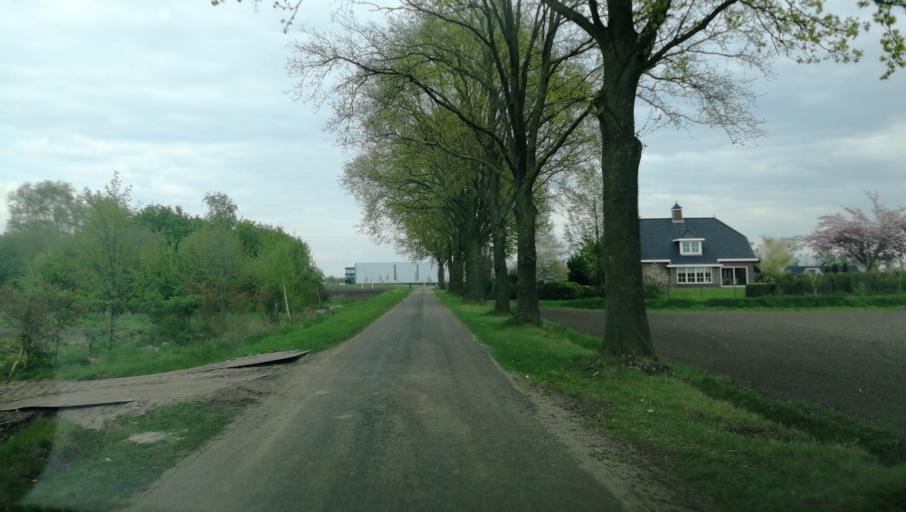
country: NL
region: Limburg
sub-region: Gemeente Peel en Maas
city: Maasbree
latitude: 51.3983
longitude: 6.0624
